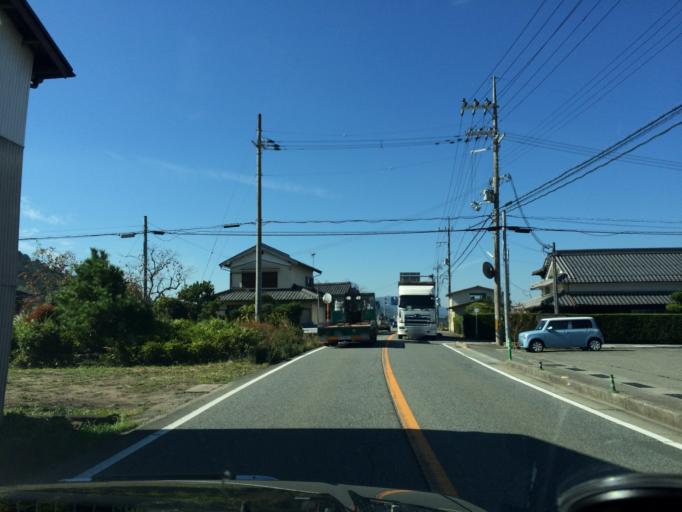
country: JP
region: Hyogo
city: Sasayama
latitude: 35.0666
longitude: 135.2489
